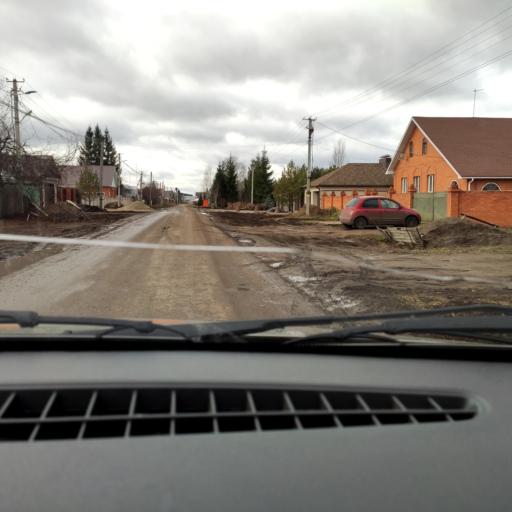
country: RU
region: Bashkortostan
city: Avdon
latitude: 54.4967
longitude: 55.8722
